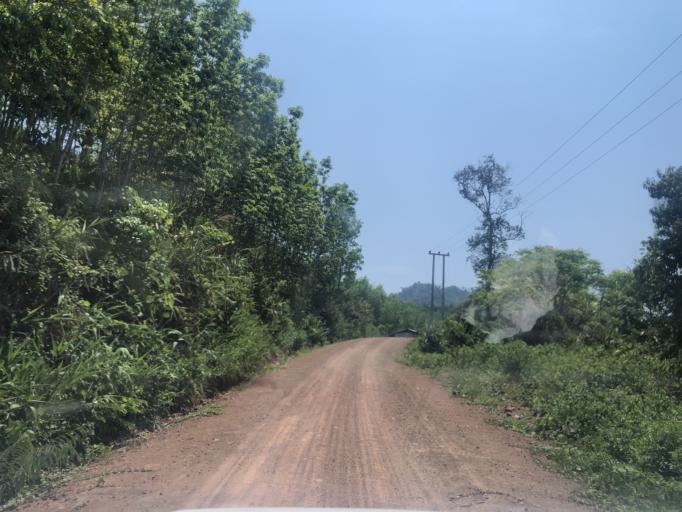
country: LA
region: Phongsali
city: Phongsali
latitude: 21.4344
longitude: 102.0338
